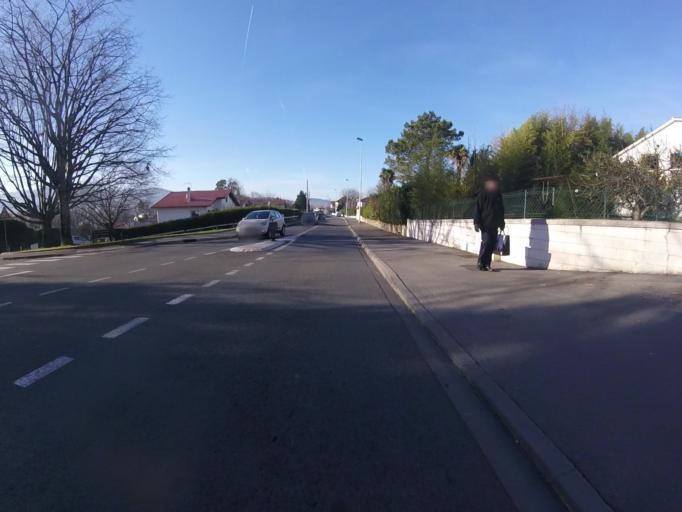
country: FR
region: Aquitaine
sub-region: Departement des Pyrenees-Atlantiques
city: Hendaye
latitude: 43.3548
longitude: -1.7687
